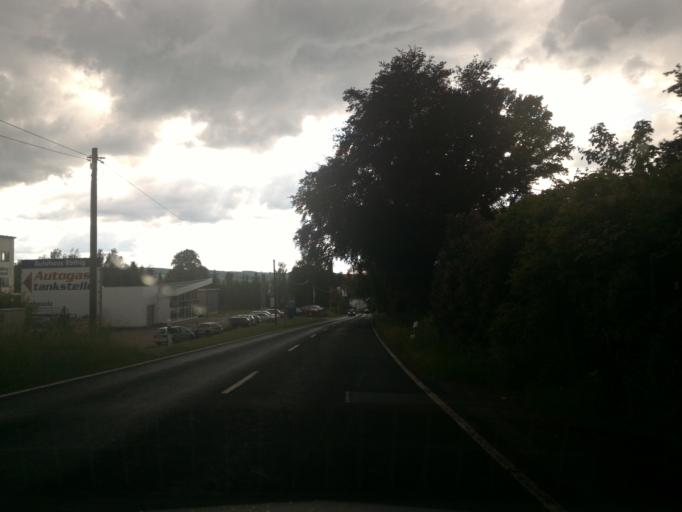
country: DE
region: Saxony
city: Seifhennersdorf
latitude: 50.9348
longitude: 14.6243
